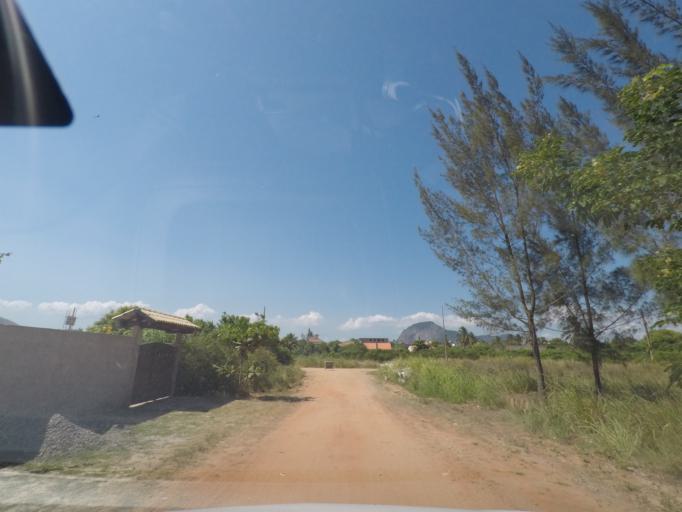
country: BR
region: Rio de Janeiro
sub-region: Marica
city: Marica
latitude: -22.9728
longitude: -42.9262
